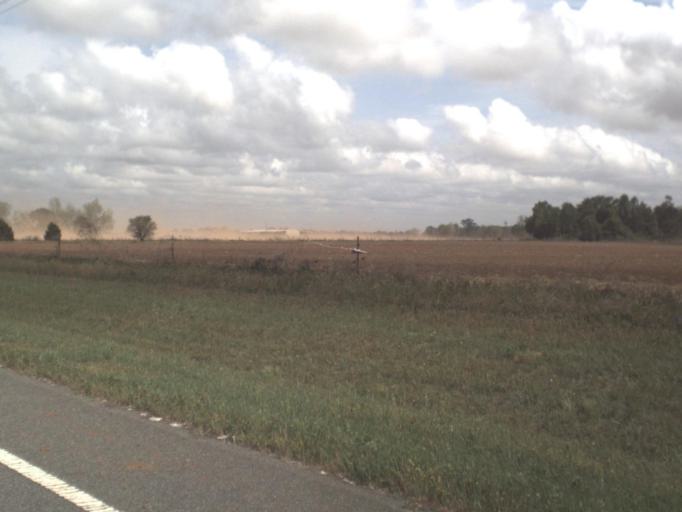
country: US
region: Florida
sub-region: Santa Rosa County
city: Point Baker
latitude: 30.8066
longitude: -87.1110
